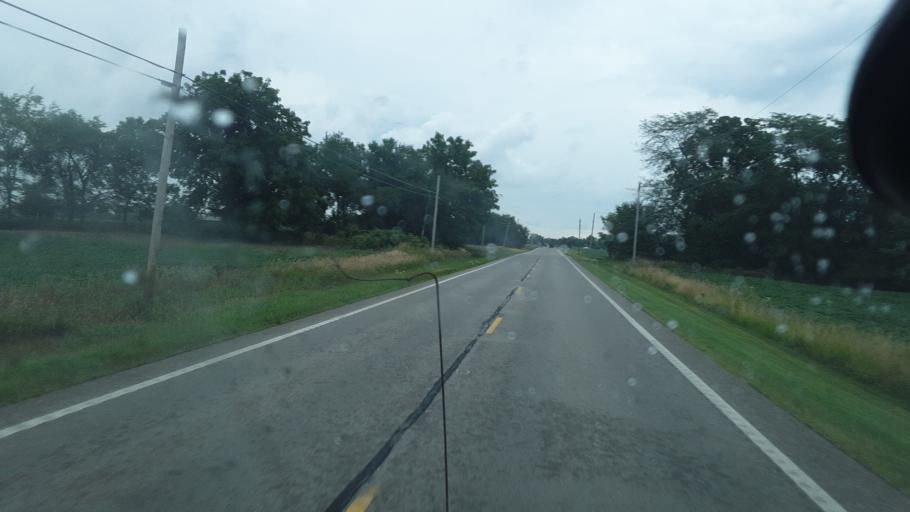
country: US
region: Ohio
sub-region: Williams County
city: Bryan
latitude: 41.4333
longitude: -84.6057
